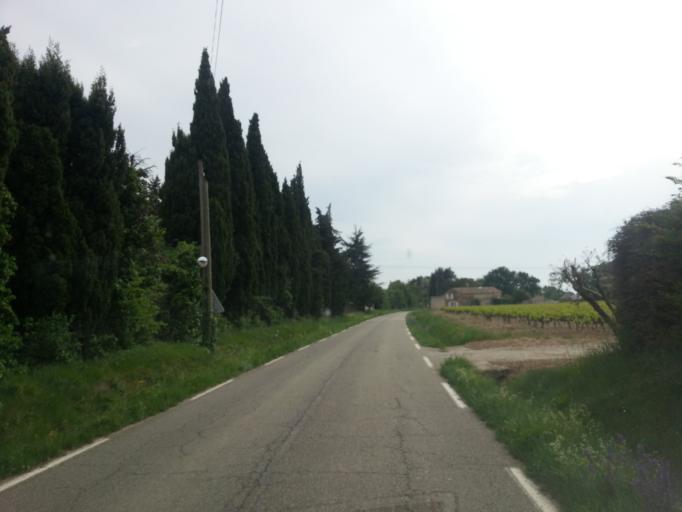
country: FR
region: Provence-Alpes-Cote d'Azur
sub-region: Departement du Vaucluse
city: Camaret-sur-Aigues
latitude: 44.1728
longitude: 4.8870
